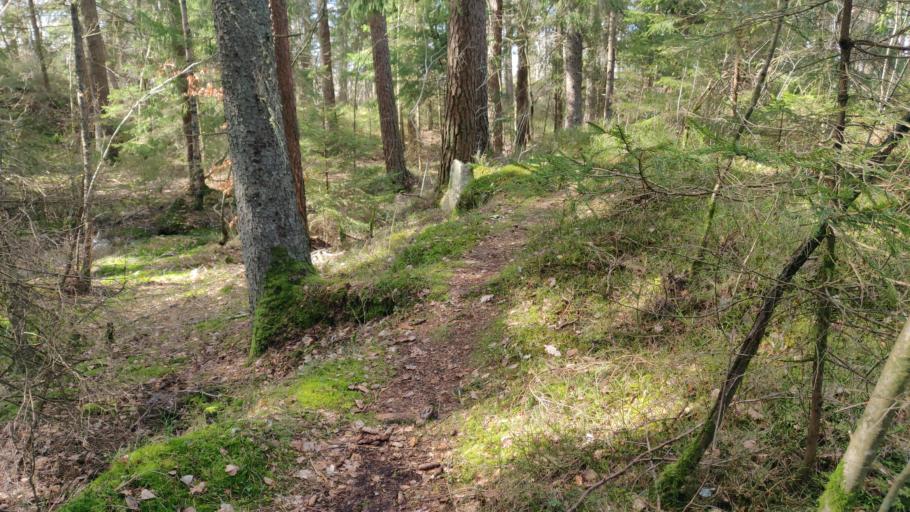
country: SE
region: Vaestra Goetaland
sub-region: Uddevalla Kommun
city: Uddevalla
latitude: 58.3403
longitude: 11.9348
